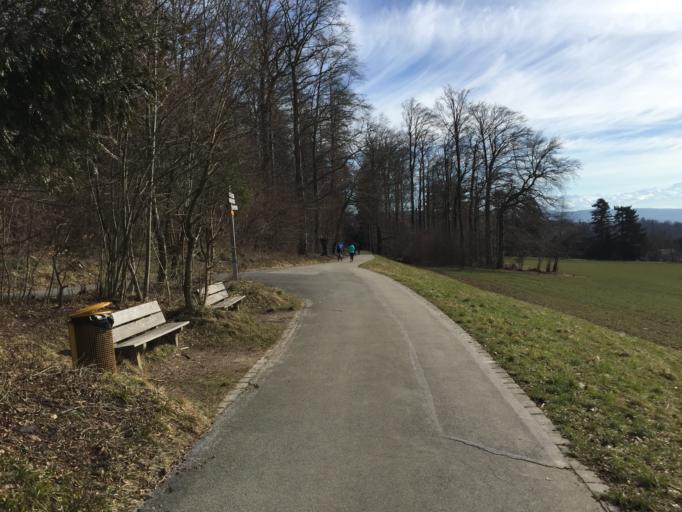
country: CH
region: Zurich
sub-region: Bezirk Zuerich
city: Zuerich (Kreis 7) / Fluntern
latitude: 47.3843
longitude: 8.5640
